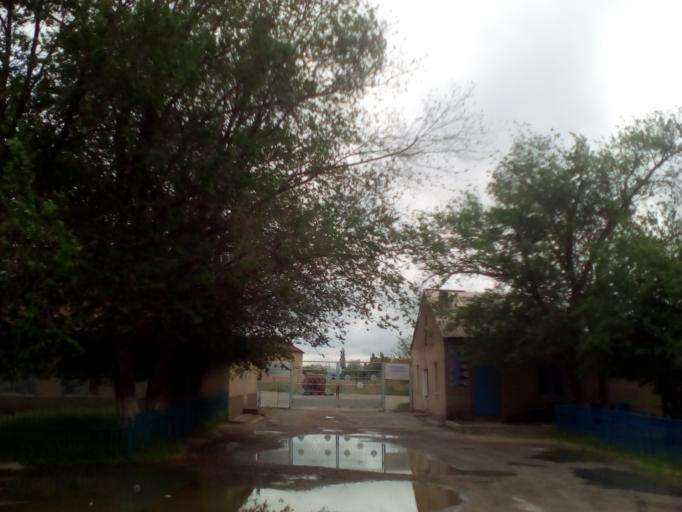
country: KZ
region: Ongtustik Qazaqstan
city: Sholaqqkorghan
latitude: 43.7585
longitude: 69.1889
